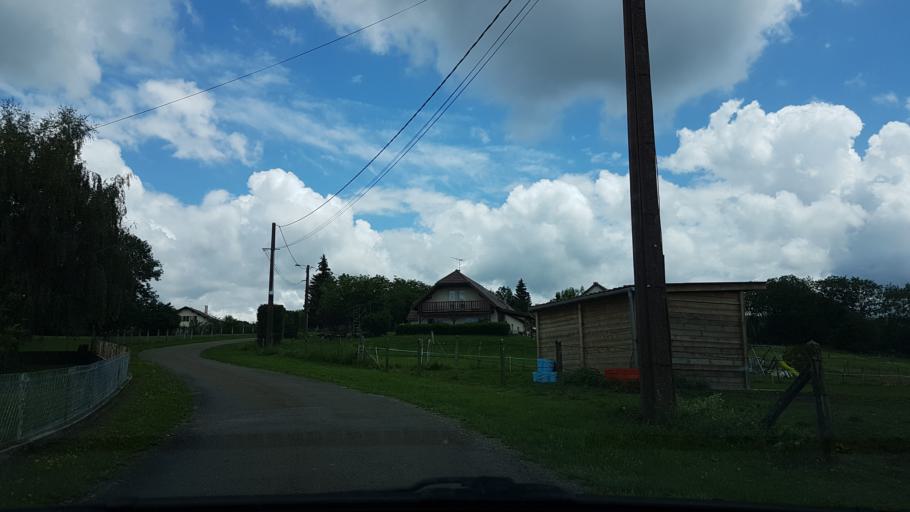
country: FR
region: Franche-Comte
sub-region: Departement du Jura
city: Clairvaux-les-Lacs
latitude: 46.5669
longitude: 5.7645
